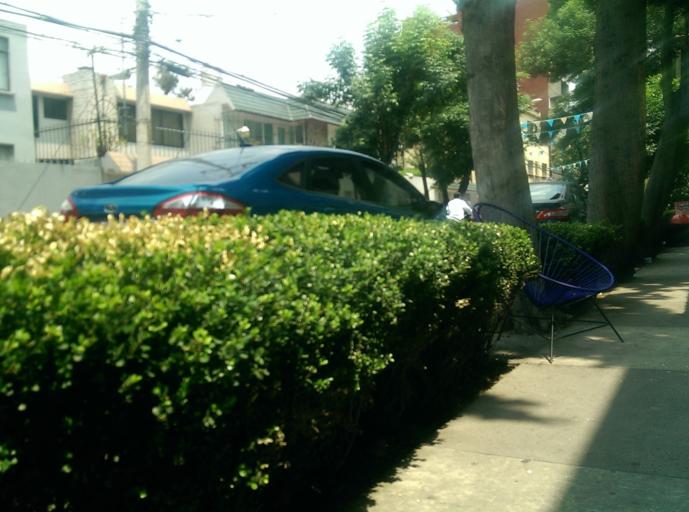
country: MX
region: Mexico City
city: Colonia del Valle
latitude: 19.3751
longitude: -99.1826
